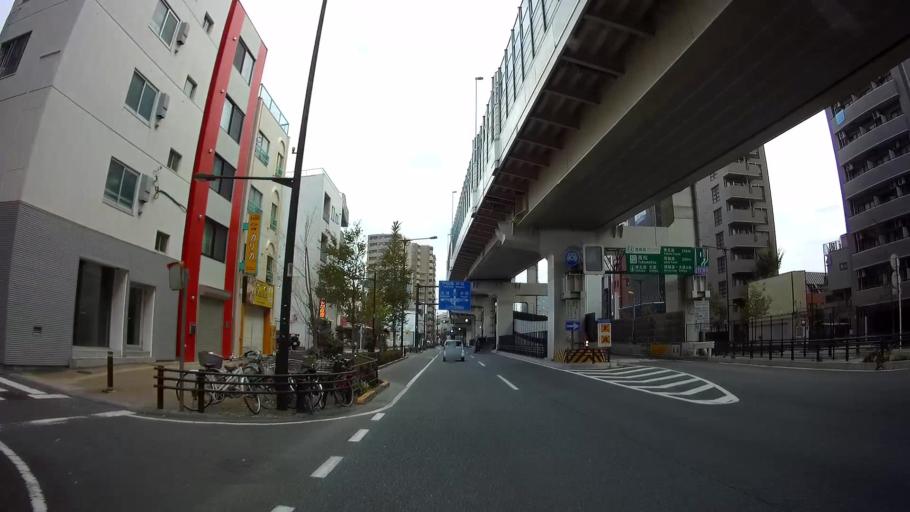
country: JP
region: Tokyo
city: Tokyo
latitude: 35.7372
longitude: 139.7026
